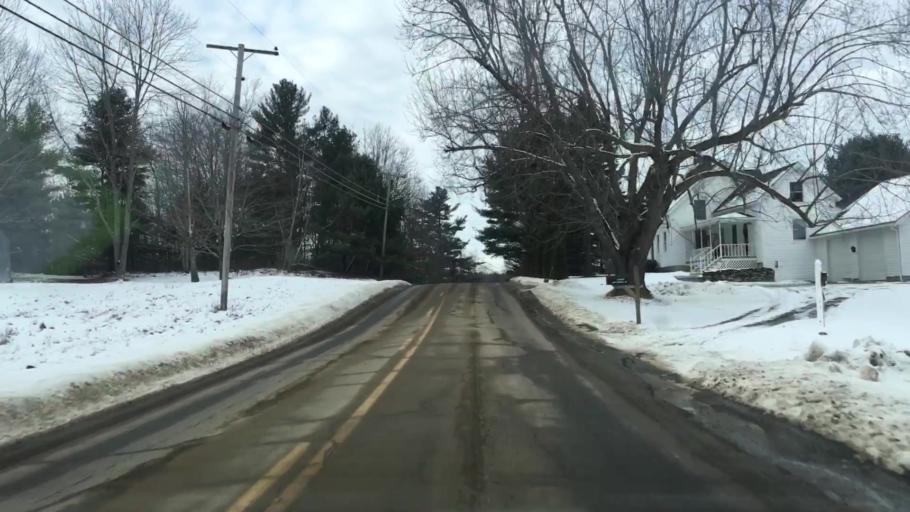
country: US
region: Maine
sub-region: Lincoln County
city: Whitefield
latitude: 44.2305
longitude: -69.6147
